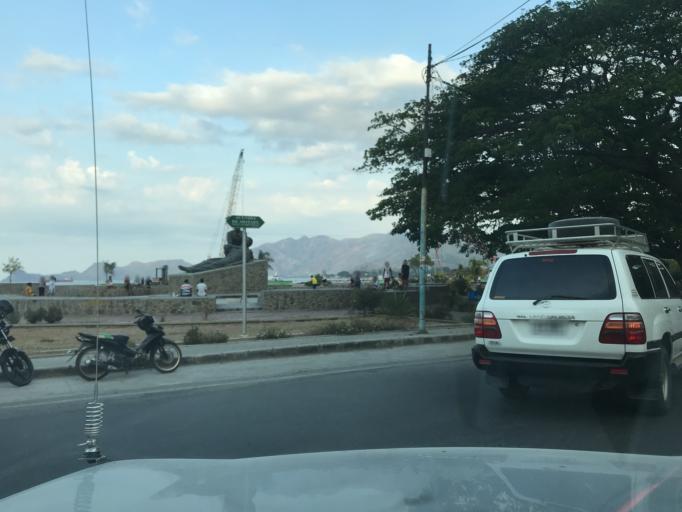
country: TL
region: Dili
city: Dili
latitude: -8.5510
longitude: 125.5710
